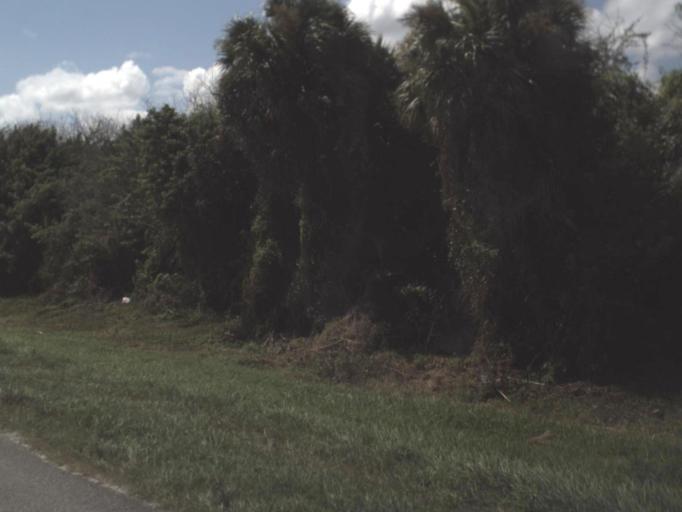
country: US
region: Florida
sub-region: Collier County
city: Immokalee
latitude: 26.5853
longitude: -81.4366
